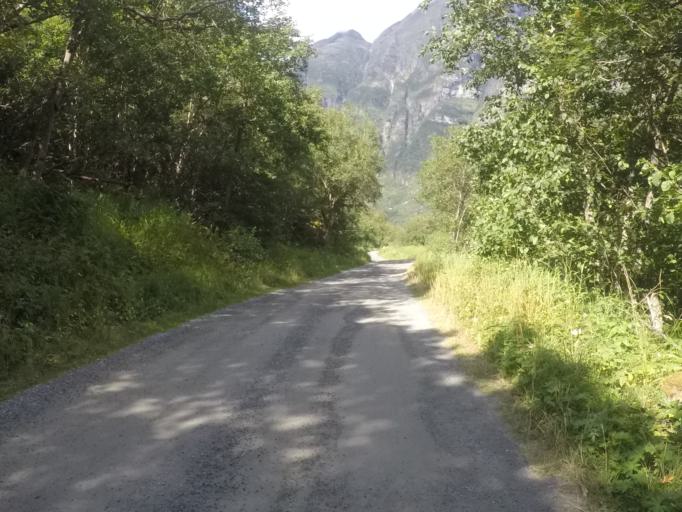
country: NO
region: Sogn og Fjordane
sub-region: Stryn
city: Stryn
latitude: 61.7500
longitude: 7.0335
